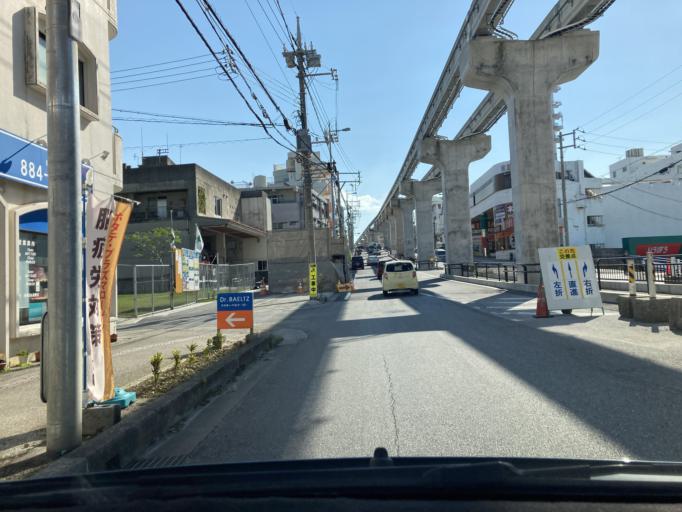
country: JP
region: Okinawa
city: Naha-shi
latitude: 26.2233
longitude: 127.7277
